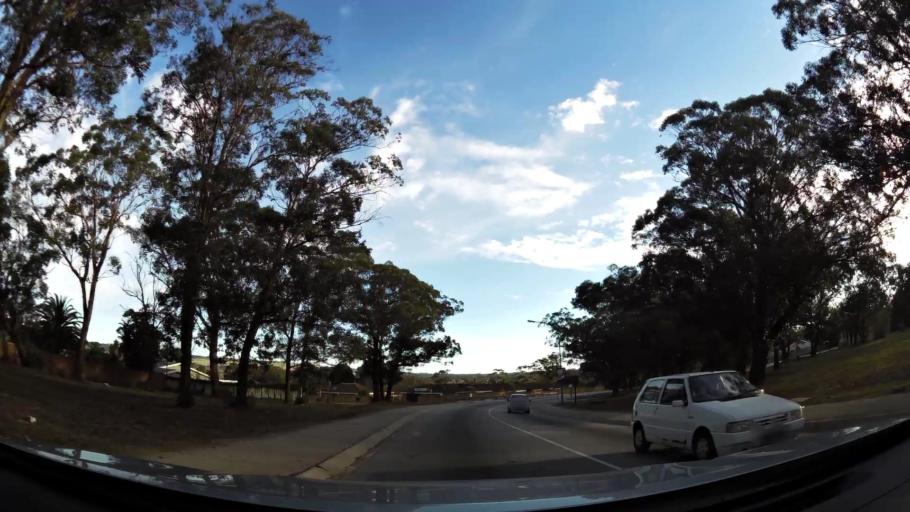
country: ZA
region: Eastern Cape
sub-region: Nelson Mandela Bay Metropolitan Municipality
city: Port Elizabeth
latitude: -33.9554
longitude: 25.5195
